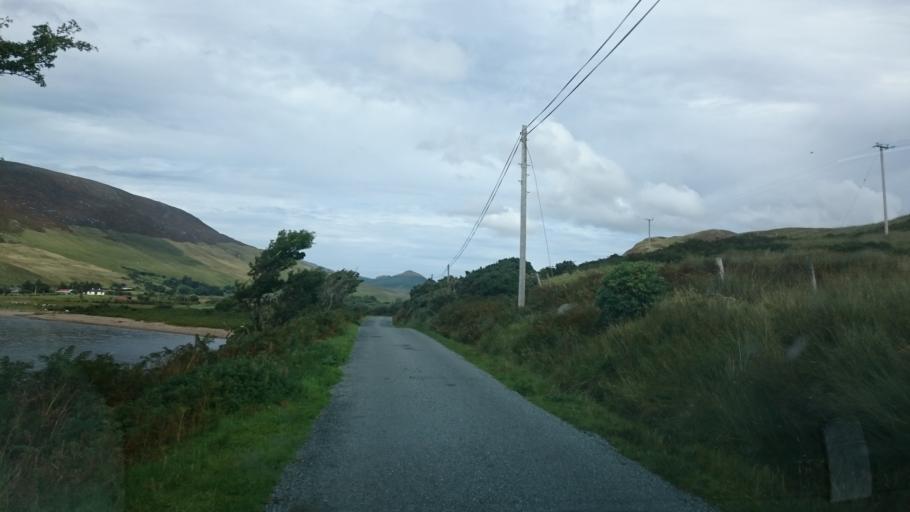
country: IE
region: Connaught
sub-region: Maigh Eo
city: Westport
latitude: 53.9555
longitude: -9.5698
